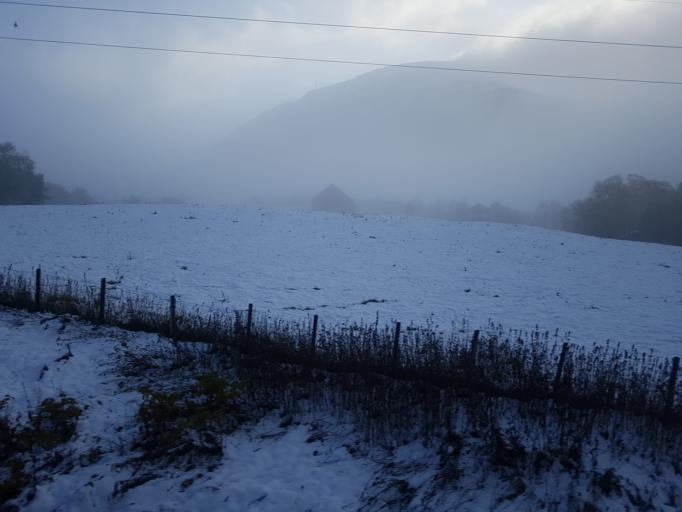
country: NO
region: Sor-Trondelag
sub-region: Oppdal
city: Oppdal
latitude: 62.5707
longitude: 9.6476
